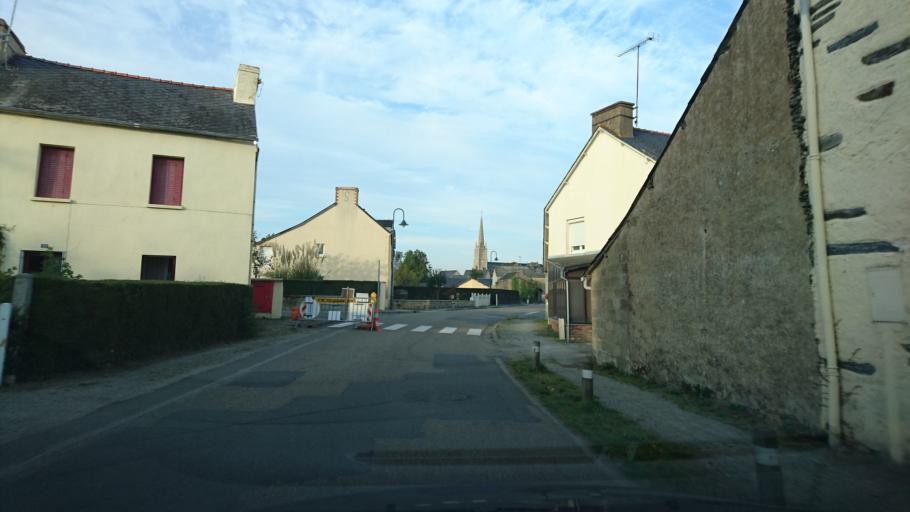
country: FR
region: Brittany
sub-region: Departement d'Ille-et-Vilaine
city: Sainte-Marie
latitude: 47.6922
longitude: -2.0031
